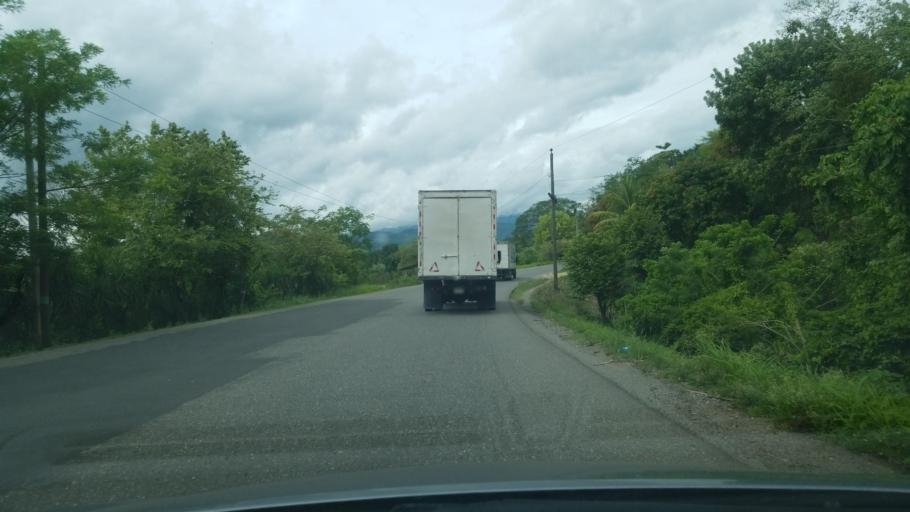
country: HN
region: Santa Barbara
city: San Marcos
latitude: 15.3099
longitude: -88.4395
